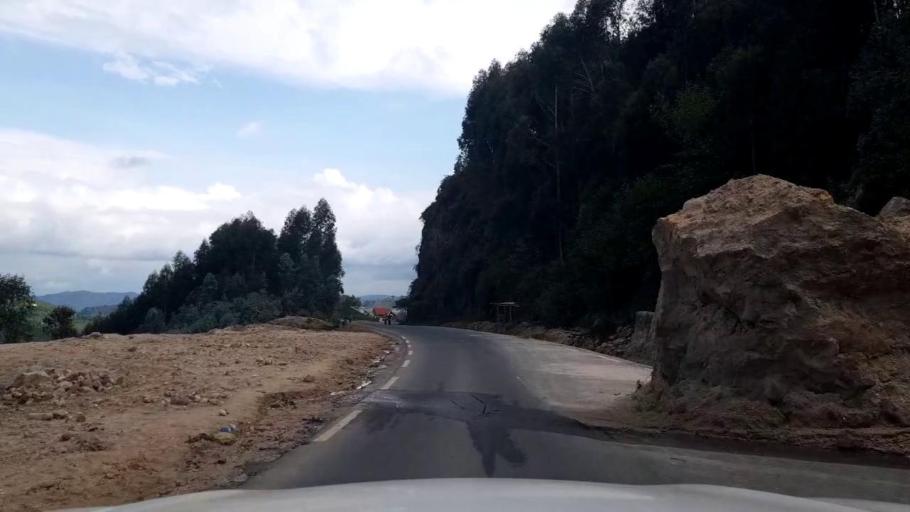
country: RW
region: Northern Province
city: Musanze
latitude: -1.6707
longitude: 29.5150
